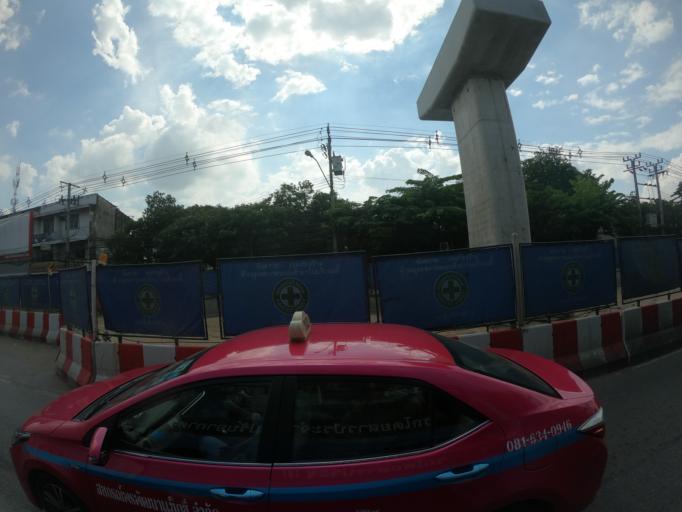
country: TH
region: Bangkok
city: Wang Thonglang
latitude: 13.7917
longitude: 100.5992
